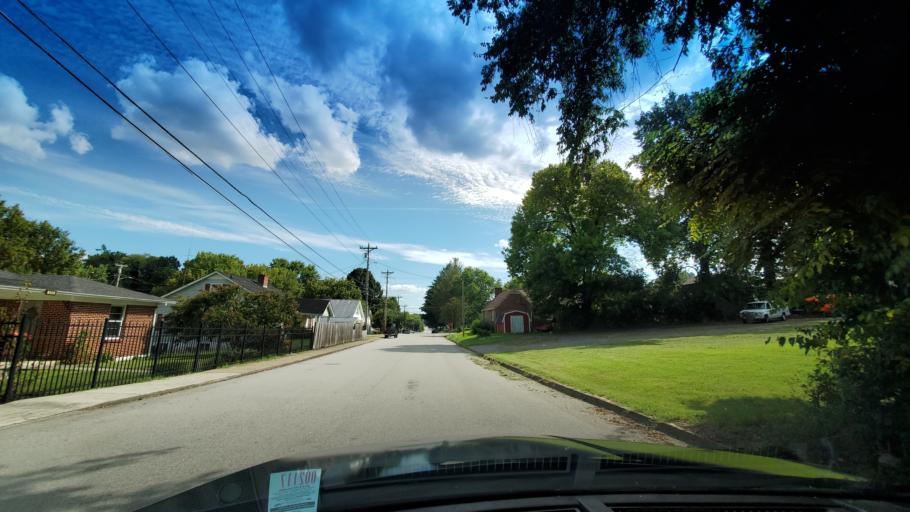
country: US
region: Tennessee
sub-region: Smith County
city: Carthage
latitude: 36.2546
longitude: -85.9505
